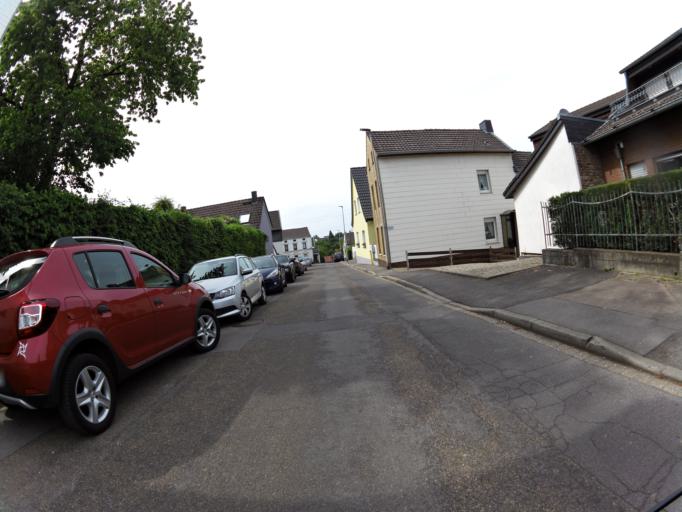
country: DE
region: North Rhine-Westphalia
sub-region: Regierungsbezirk Koln
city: Herzogenrath
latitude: 50.8446
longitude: 6.0862
